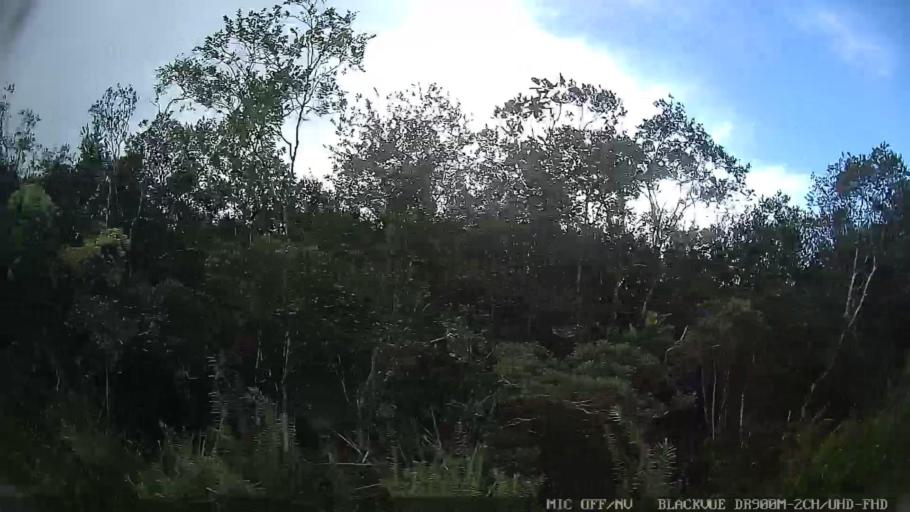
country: BR
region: Sao Paulo
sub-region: Peruibe
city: Peruibe
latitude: -24.2025
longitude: -46.9341
